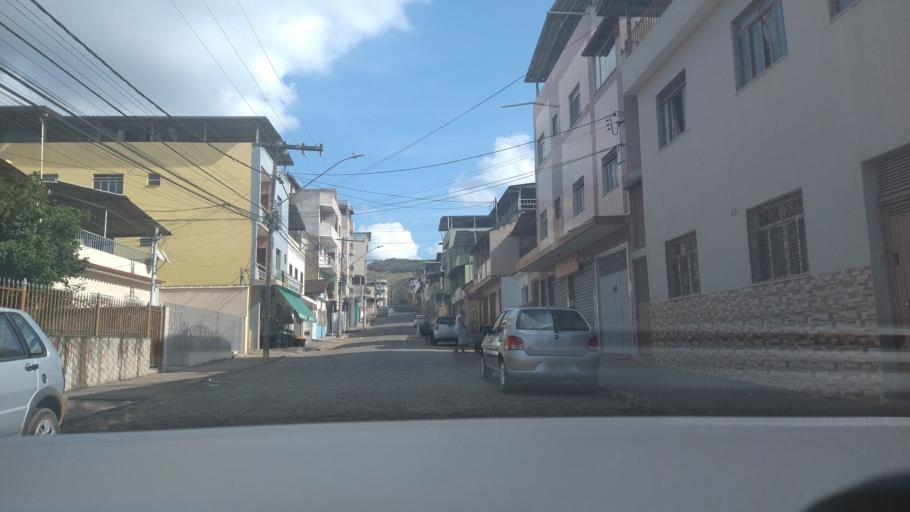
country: BR
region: Minas Gerais
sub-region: Vicosa
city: Vicosa
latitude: -20.7657
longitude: -42.8859
